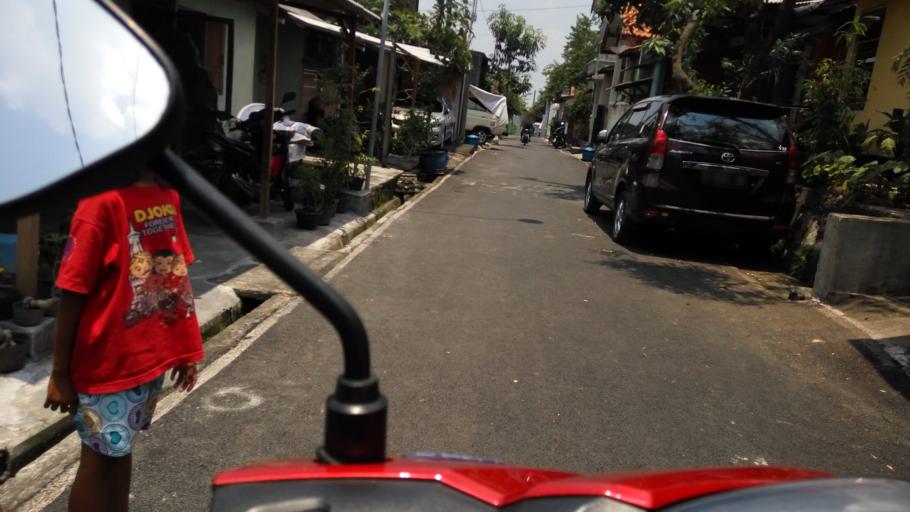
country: ID
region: Central Java
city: Mranggen
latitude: -7.0444
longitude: 110.4750
